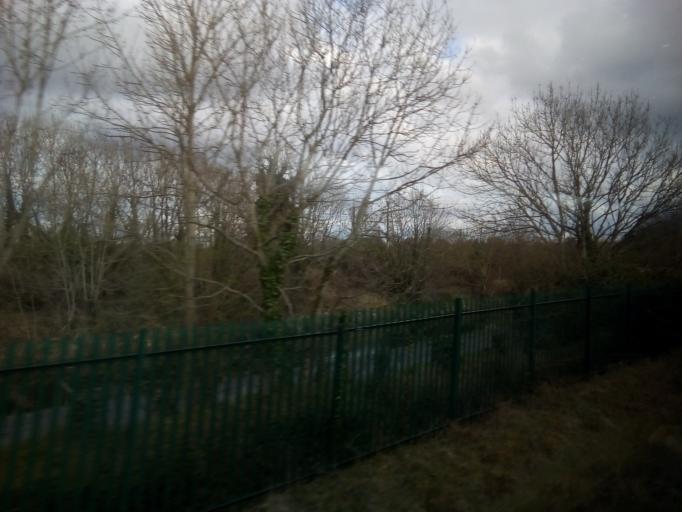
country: IE
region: Leinster
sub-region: An Iarmhi
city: An Muileann gCearr
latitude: 53.5156
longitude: -7.3260
